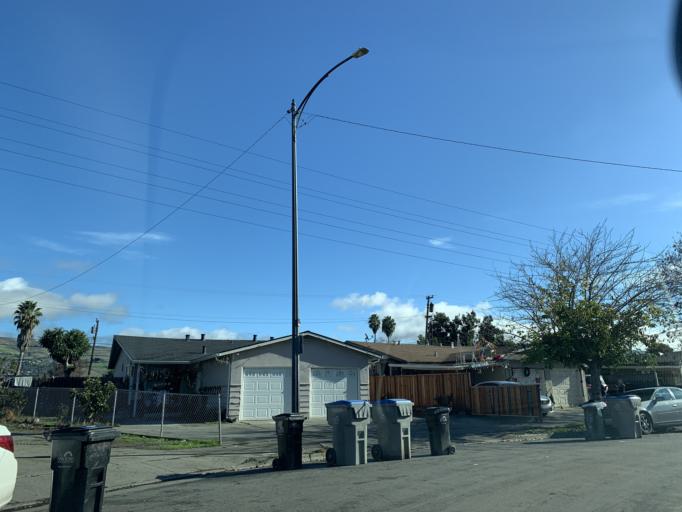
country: US
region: California
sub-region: Santa Clara County
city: Alum Rock
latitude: 37.3546
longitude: -121.8354
